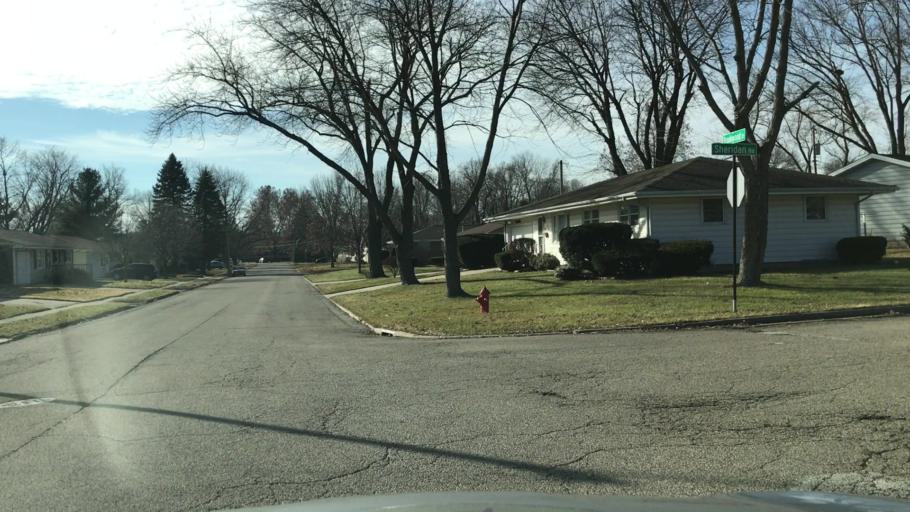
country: US
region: Illinois
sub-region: McLean County
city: Normal
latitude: 40.5021
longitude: -88.9640
